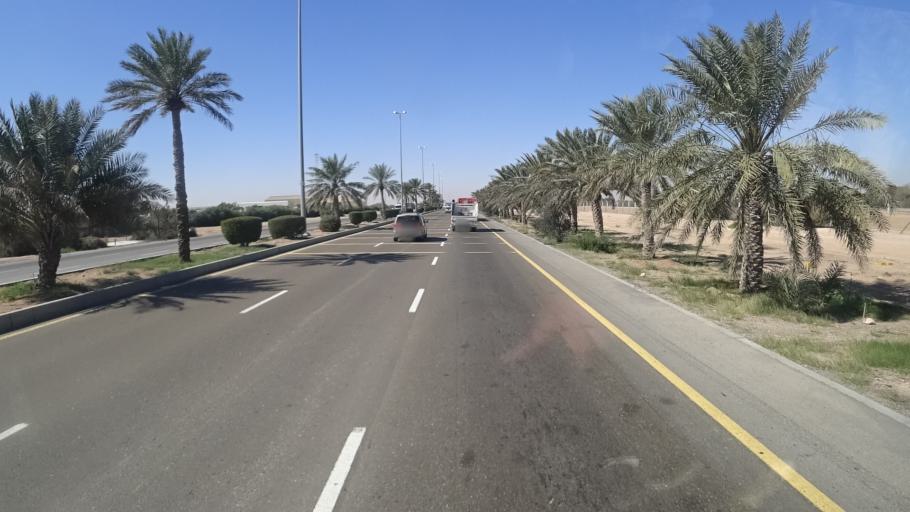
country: AE
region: Abu Dhabi
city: Al Ain
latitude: 24.0811
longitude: 55.6682
